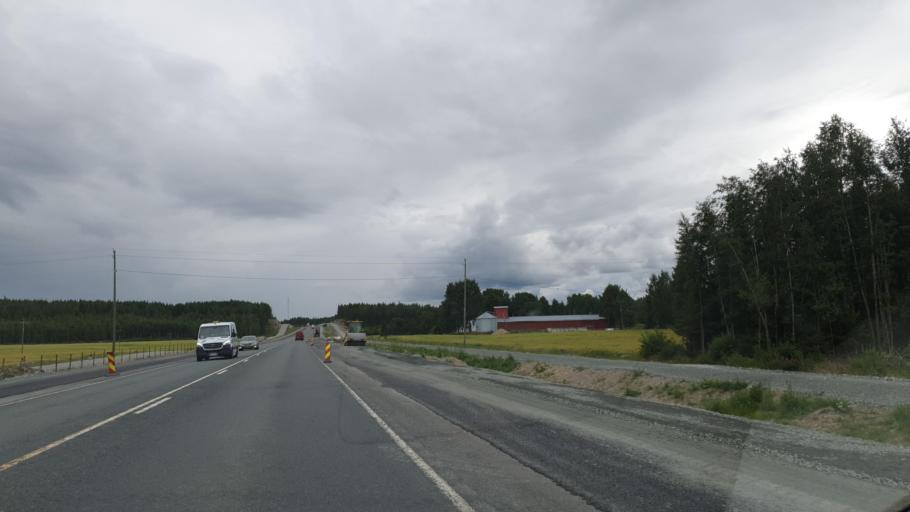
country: FI
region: Northern Savo
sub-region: Ylae-Savo
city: Lapinlahti
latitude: 63.2902
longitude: 27.4542
